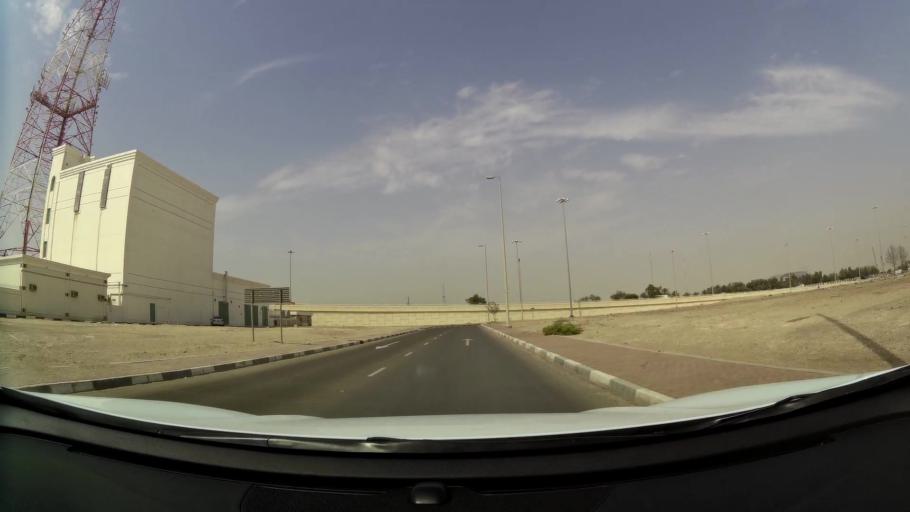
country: AE
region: Abu Dhabi
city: Abu Dhabi
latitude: 24.3129
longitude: 54.6061
